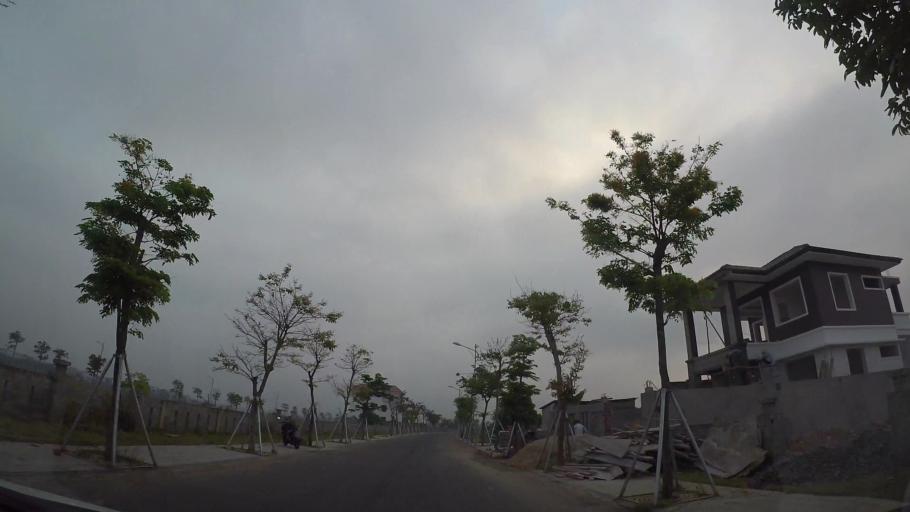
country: VN
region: Da Nang
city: Cam Le
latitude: 16.0254
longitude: 108.2287
